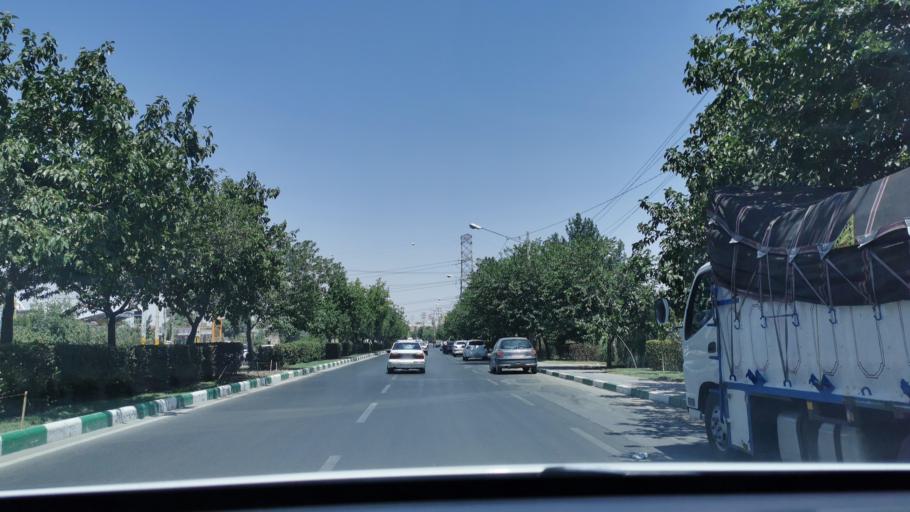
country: IR
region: Razavi Khorasan
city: Mashhad
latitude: 36.3487
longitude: 59.6284
